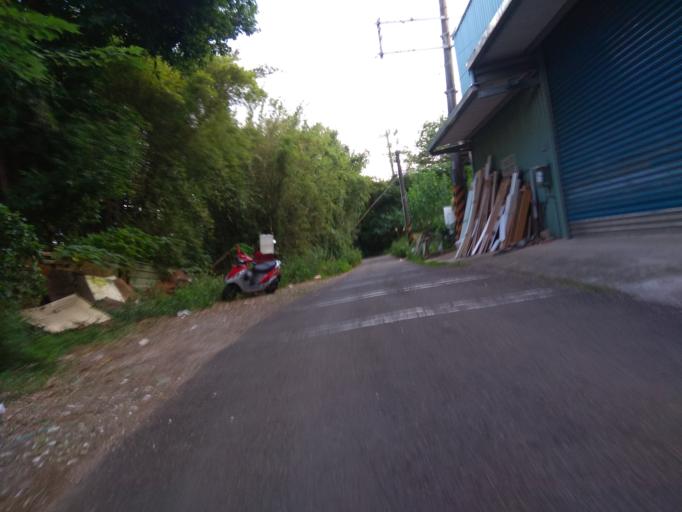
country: TW
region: Taiwan
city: Daxi
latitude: 24.9294
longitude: 121.1889
